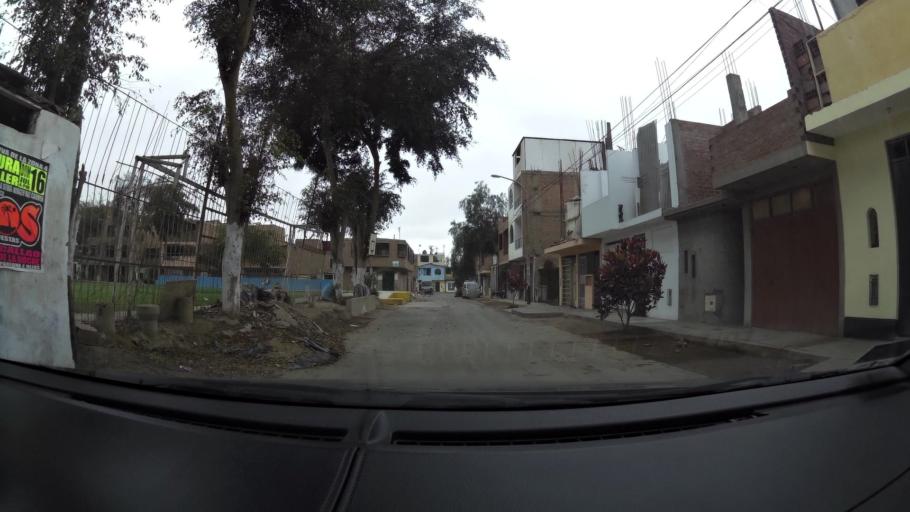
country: PE
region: Lima
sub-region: Lima
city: Independencia
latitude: -11.9659
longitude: -77.0771
